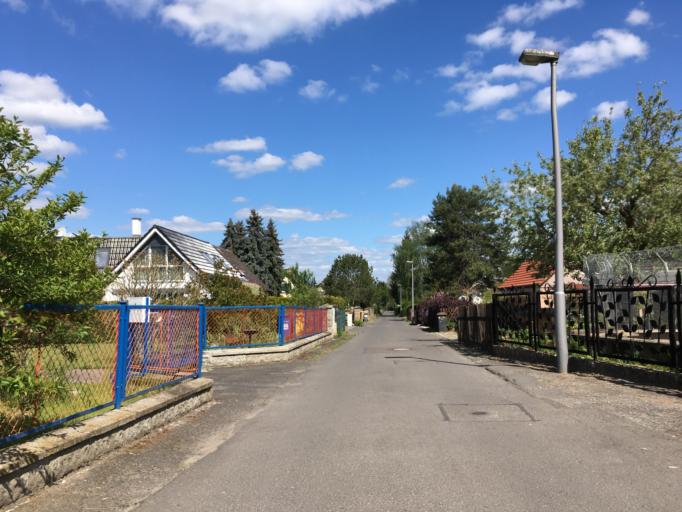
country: DE
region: Berlin
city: Blankenfelde
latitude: 52.6280
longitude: 13.3867
